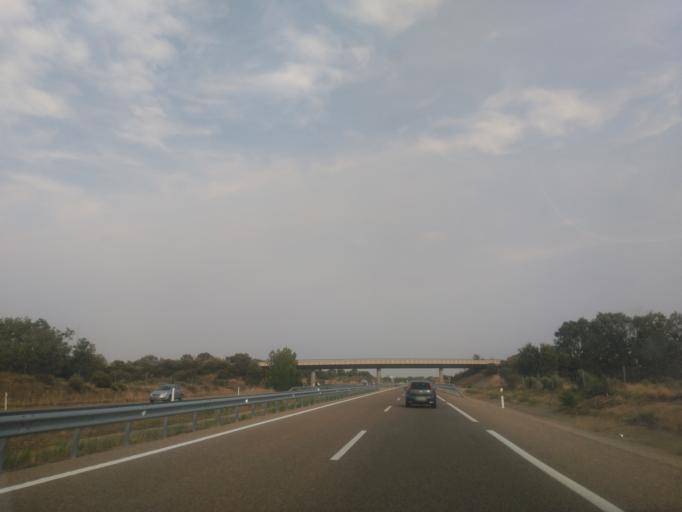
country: ES
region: Castille and Leon
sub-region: Provincia de Zamora
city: Mombuey
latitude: 42.0164
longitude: -6.3120
